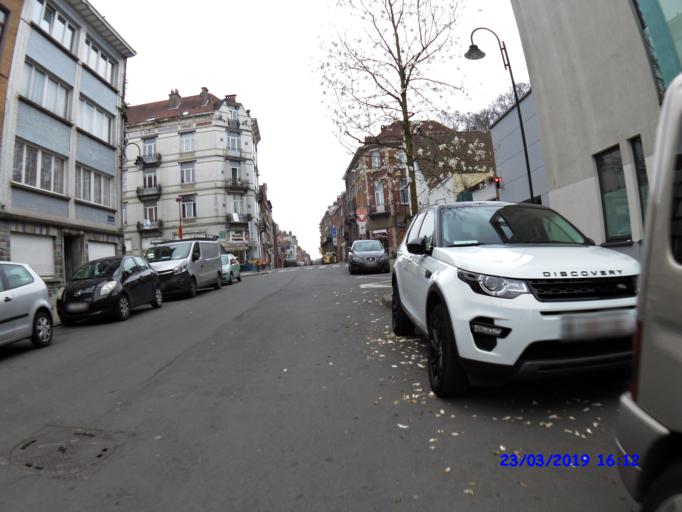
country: BE
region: Brussels Capital
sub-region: Bruxelles-Capitale
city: Brussels
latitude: 50.8768
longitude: 4.3381
